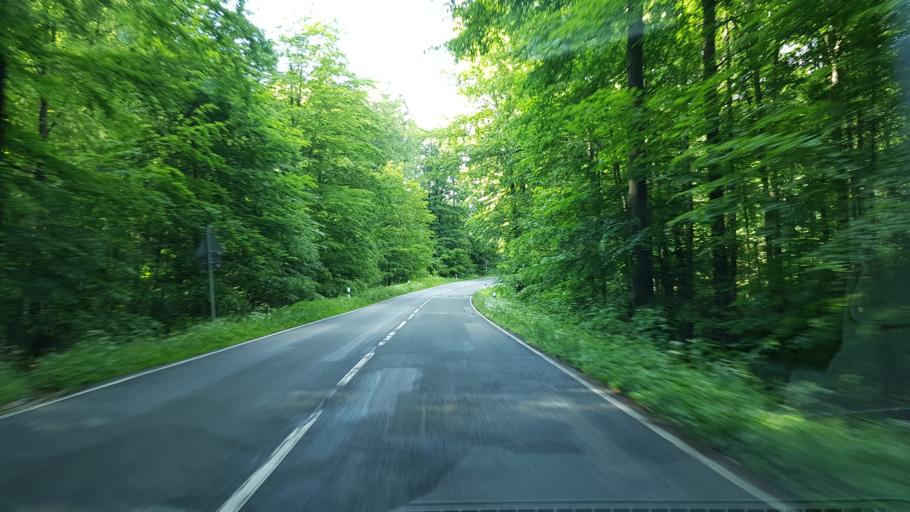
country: DE
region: Lower Saxony
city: Coppengrave
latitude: 51.9570
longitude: 9.7582
